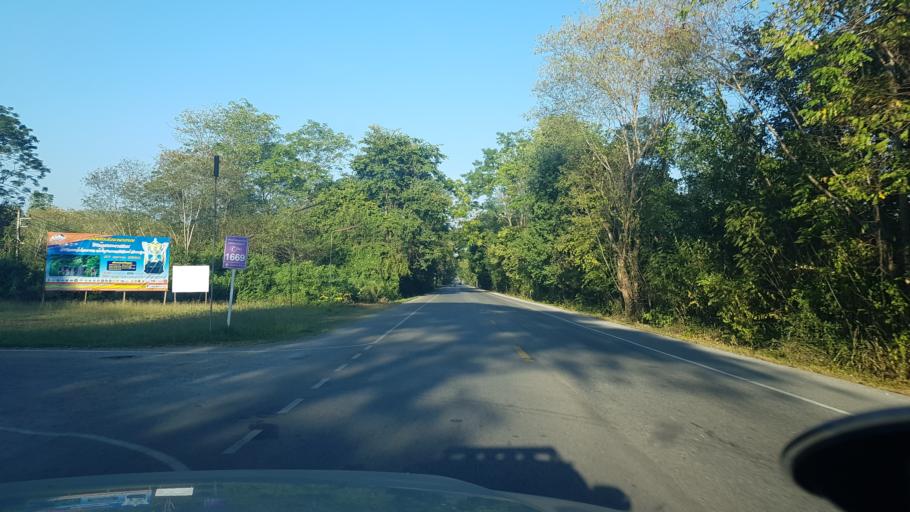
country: TH
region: Khon Kaen
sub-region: Amphoe Phu Pha Man
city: Phu Pha Man
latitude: 16.6256
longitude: 101.8526
